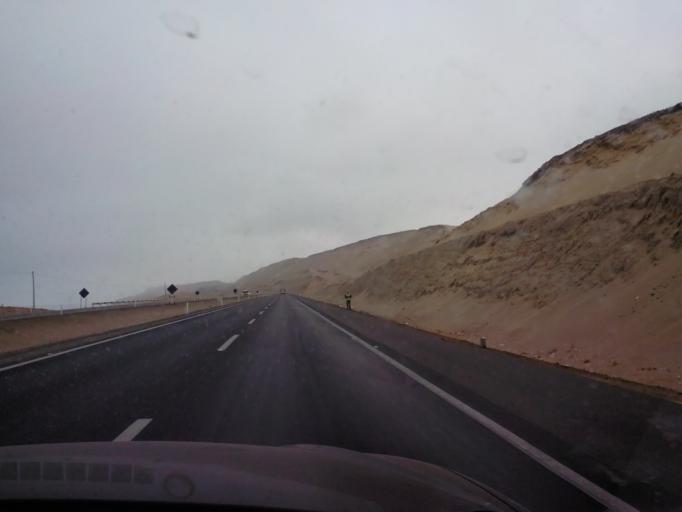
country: PE
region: Ica
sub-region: Provincia de Chincha
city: San Pedro
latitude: -13.3143
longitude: -76.2476
